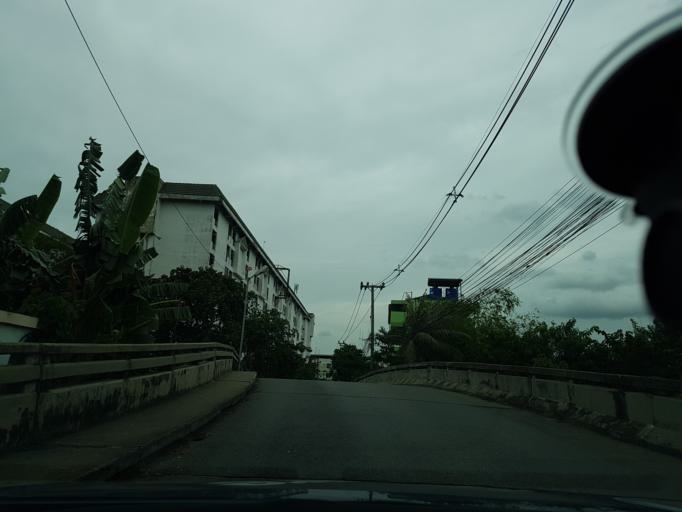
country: TH
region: Bangkok
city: Sai Mai
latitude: 13.9751
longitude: 100.6220
